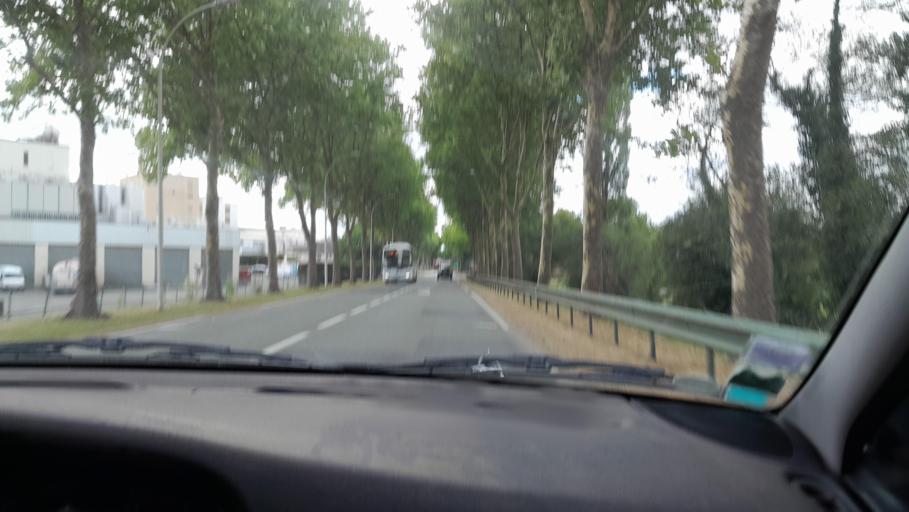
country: FR
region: Pays de la Loire
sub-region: Departement de la Mayenne
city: Craon
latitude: 47.8432
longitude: -0.9565
